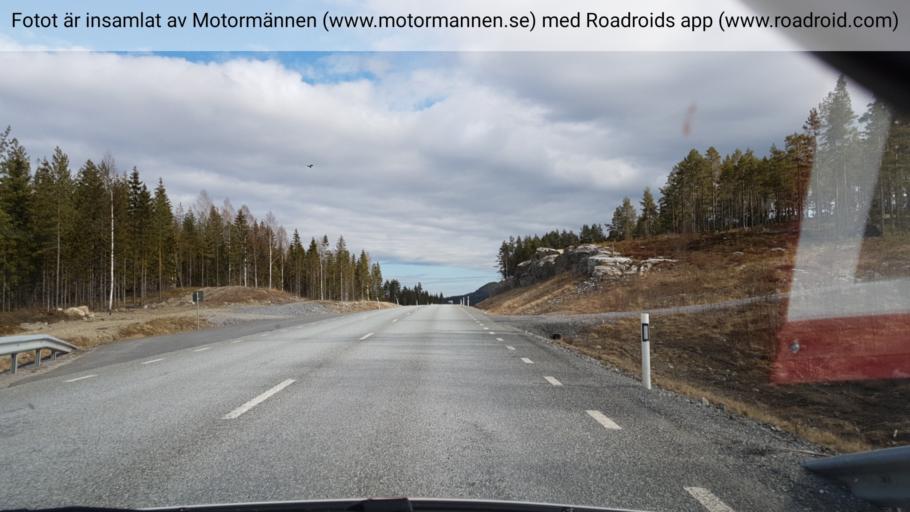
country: SE
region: Vaesternorrland
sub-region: Kramfors Kommun
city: Bollstabruk
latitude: 63.0554
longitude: 17.6128
